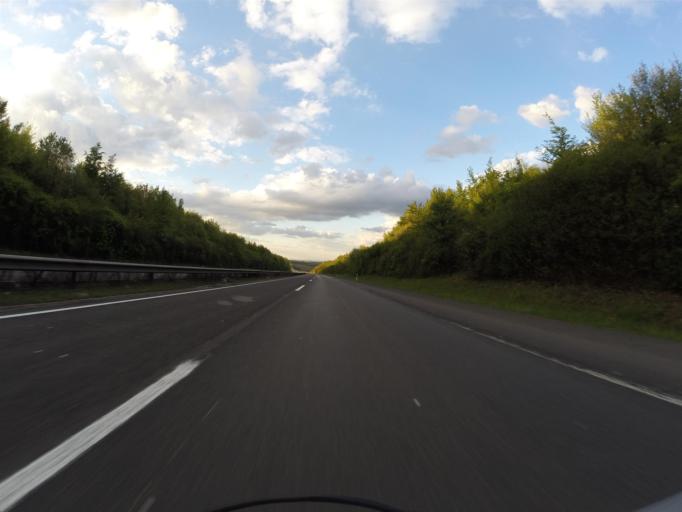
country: DE
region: Rheinland-Pfalz
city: Freimersheim
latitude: 49.7242
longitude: 8.0795
